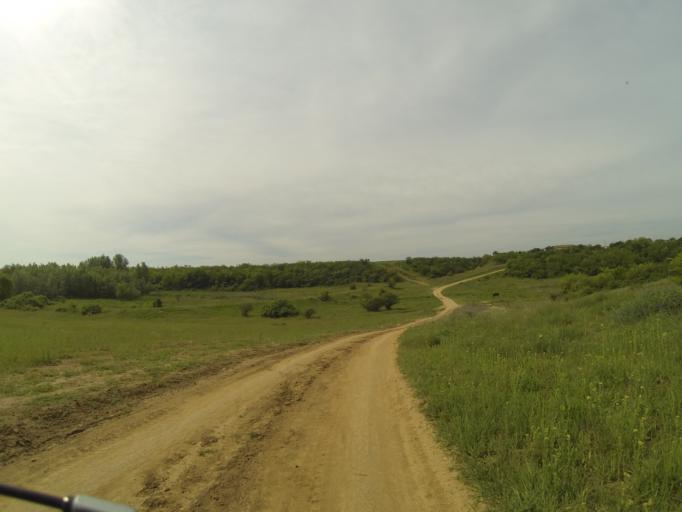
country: RO
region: Dolj
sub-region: Comuna Malu Mare
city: Preajba
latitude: 44.2649
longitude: 23.8641
